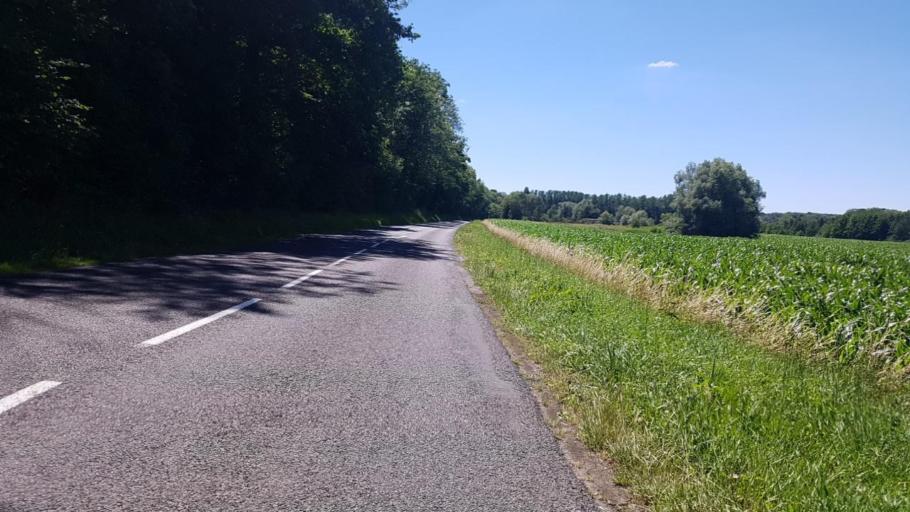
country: FR
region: Ile-de-France
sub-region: Departement de Seine-et-Marne
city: Fublaines
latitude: 48.9374
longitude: 2.9174
